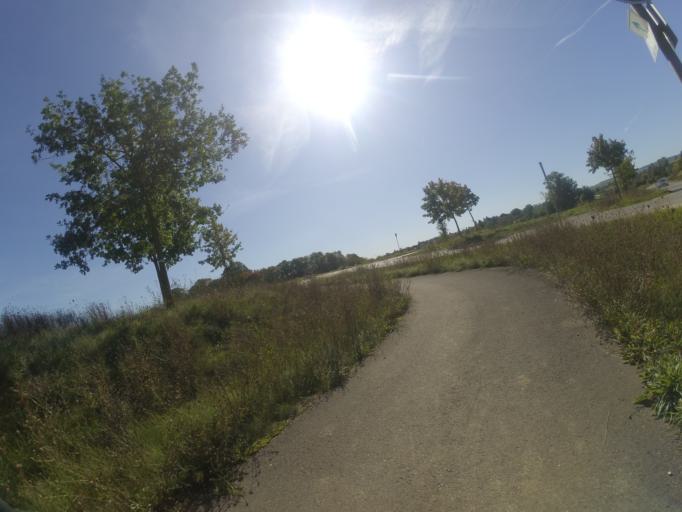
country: DE
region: Baden-Wuerttemberg
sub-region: Tuebingen Region
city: Langenau
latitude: 48.5011
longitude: 10.1025
